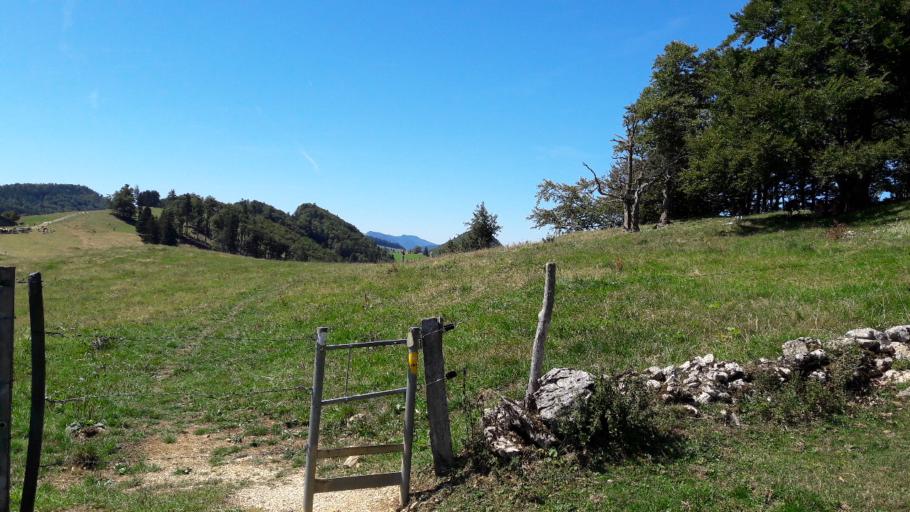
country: CH
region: Solothurn
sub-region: Bezirk Thal
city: Welschenrohr
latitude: 47.3139
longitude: 7.5678
